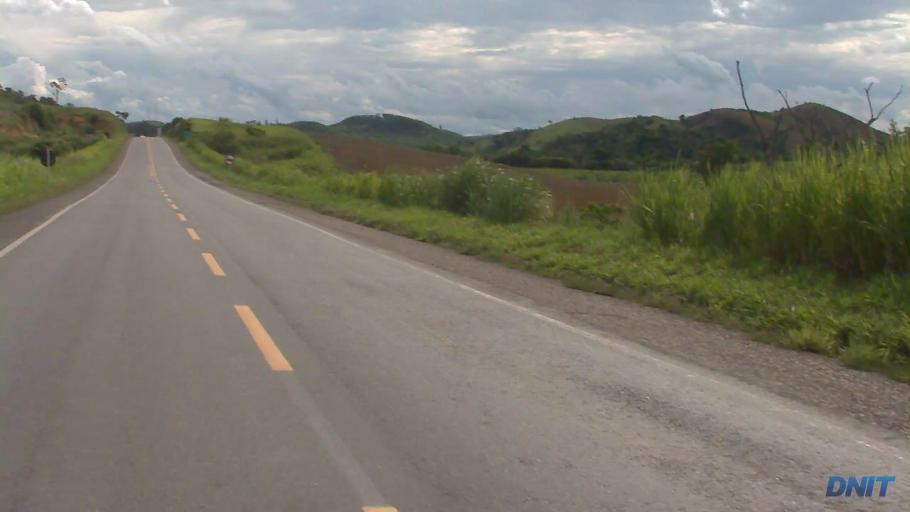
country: BR
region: Minas Gerais
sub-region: Belo Oriente
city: Belo Oriente
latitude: -19.1986
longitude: -42.2857
